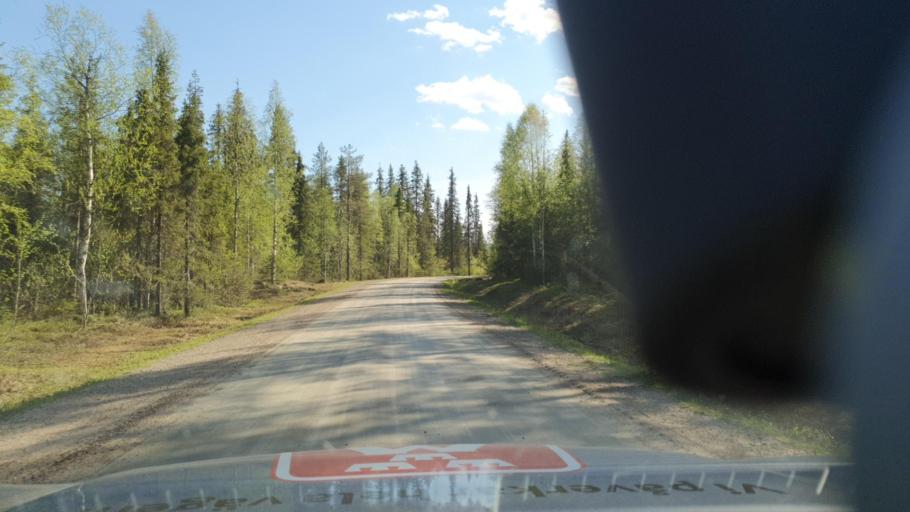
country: SE
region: Norrbotten
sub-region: Bodens Kommun
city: Boden
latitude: 66.3868
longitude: 21.6183
